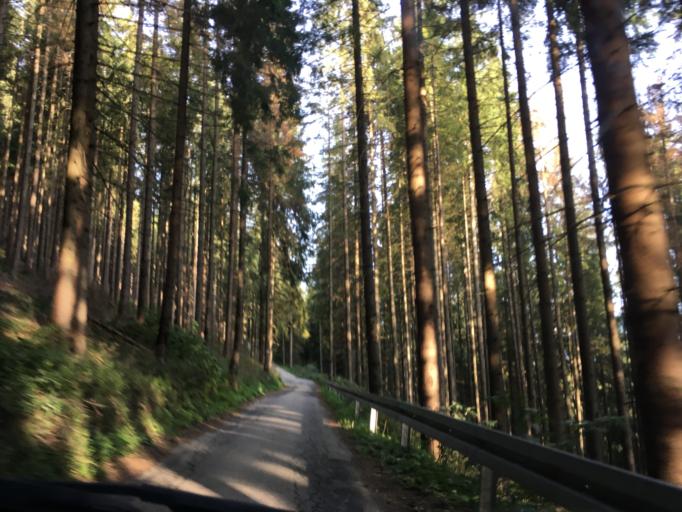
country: PL
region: Lesser Poland Voivodeship
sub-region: Powiat tatrzanski
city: Koscielisko
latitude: 49.3088
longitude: 19.8391
